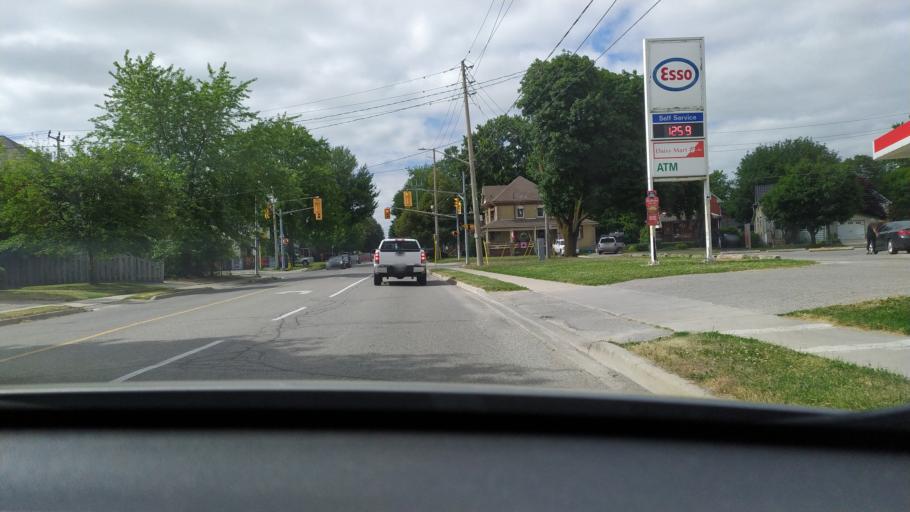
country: CA
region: Ontario
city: Stratford
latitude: 43.3598
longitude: -80.9762
